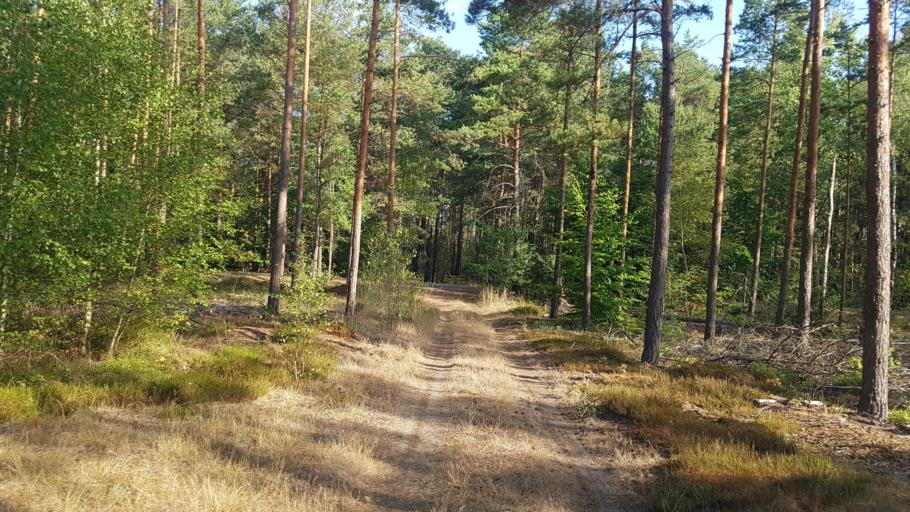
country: DE
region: Brandenburg
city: Sallgast
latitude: 51.5766
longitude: 13.8254
